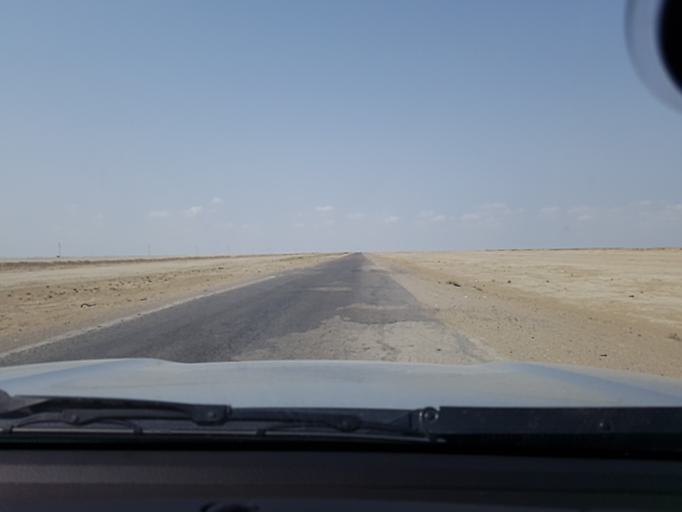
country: TM
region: Balkan
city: Gumdag
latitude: 38.6710
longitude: 54.4059
